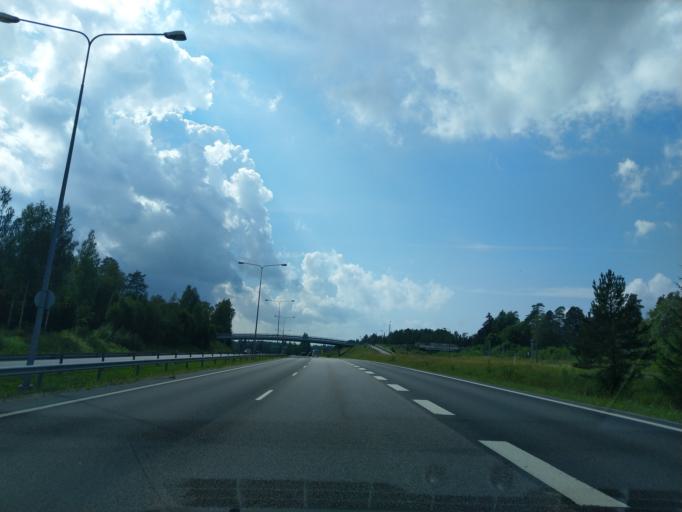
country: FI
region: South Karelia
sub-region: Imatra
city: Imatra
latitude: 61.1996
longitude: 28.7974
